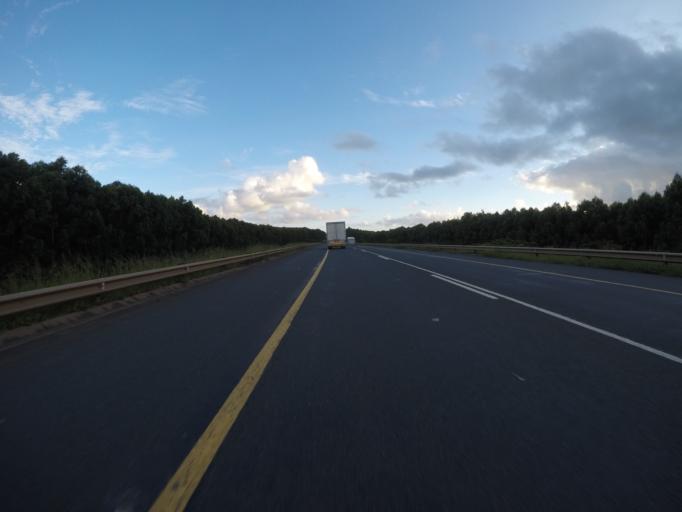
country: ZA
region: KwaZulu-Natal
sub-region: uThungulu District Municipality
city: KwaMbonambi
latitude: -28.5834
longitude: 32.0989
